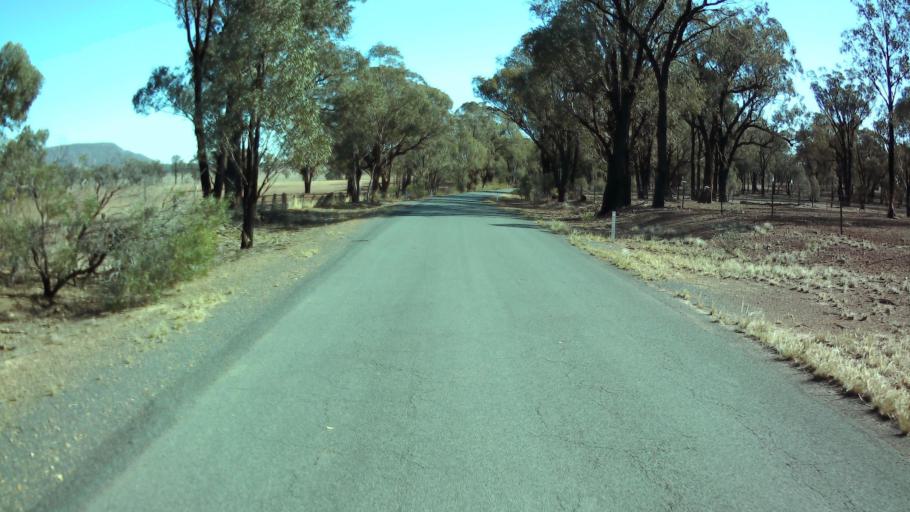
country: AU
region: New South Wales
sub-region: Weddin
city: Grenfell
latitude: -33.7862
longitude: 147.9583
